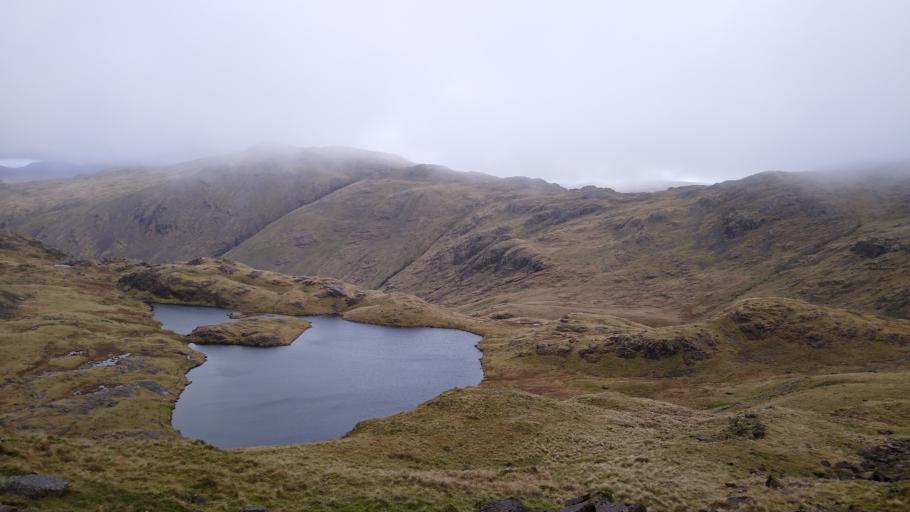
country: GB
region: England
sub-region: Cumbria
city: Keswick
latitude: 54.4701
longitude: -3.1967
